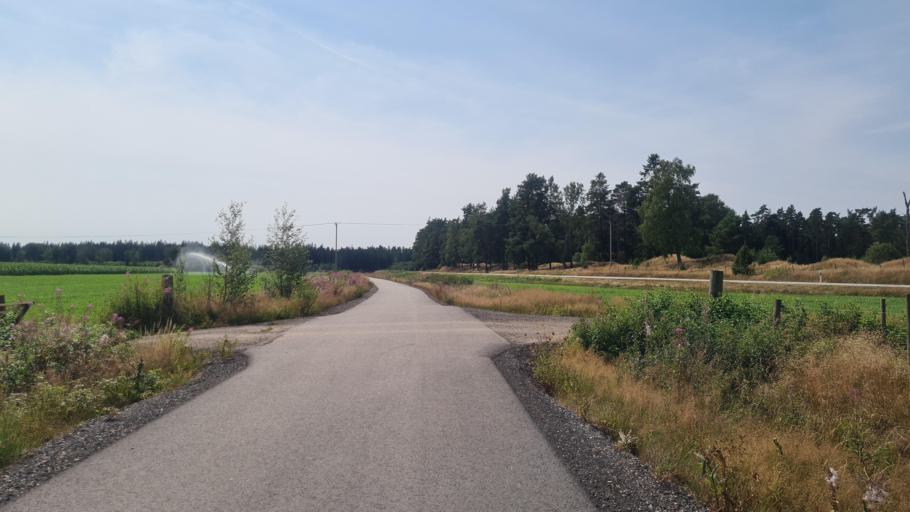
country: SE
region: Kronoberg
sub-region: Ljungby Kommun
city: Lagan
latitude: 56.8704
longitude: 13.9793
